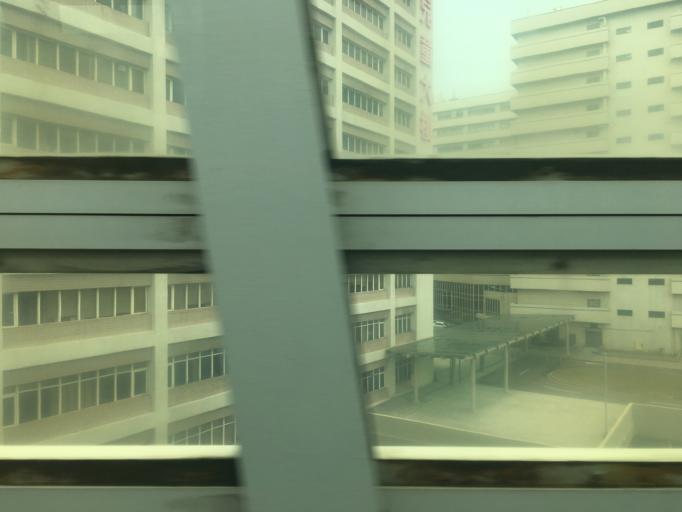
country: TW
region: Taiwan
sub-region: Taoyuan
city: Taoyuan
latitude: 25.0616
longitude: 121.3697
